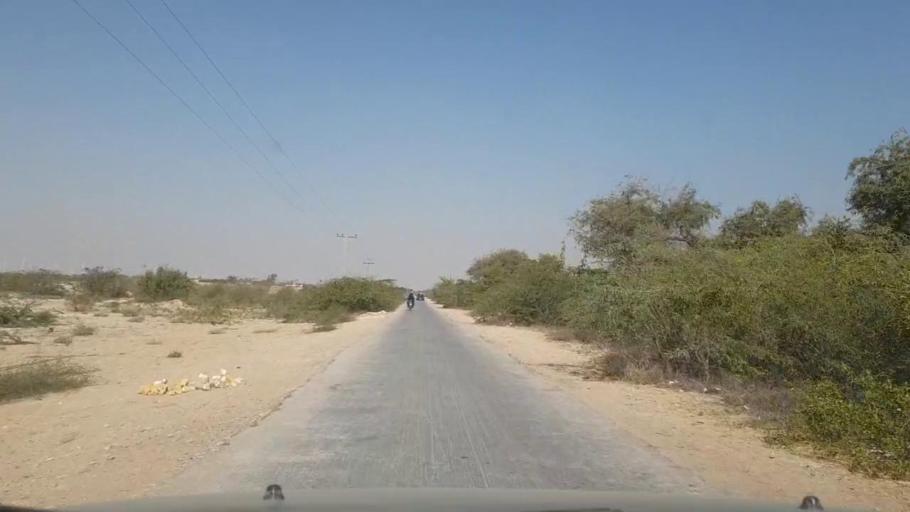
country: PK
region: Sindh
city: Daro Mehar
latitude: 25.0048
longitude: 68.0139
